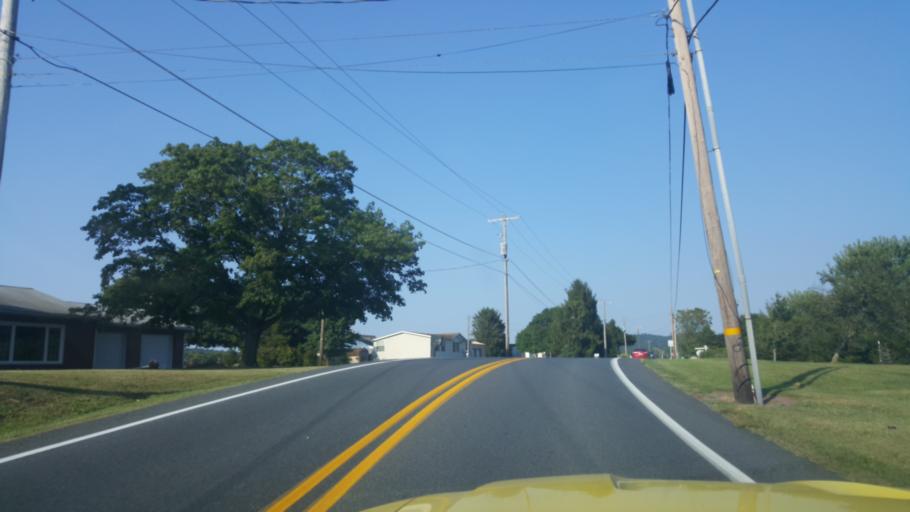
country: US
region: Pennsylvania
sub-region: Lebanon County
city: Campbelltown
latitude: 40.2334
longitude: -76.5321
